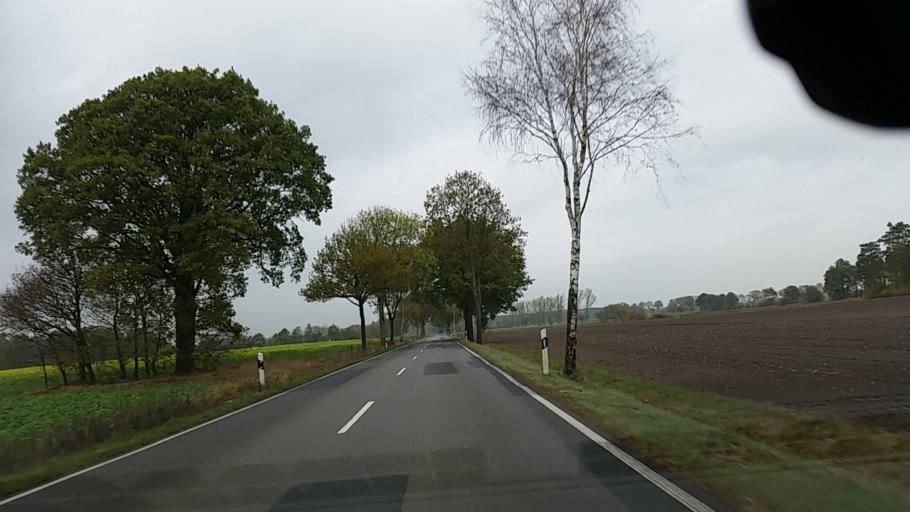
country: DE
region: Lower Saxony
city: Tulau
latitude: 52.6442
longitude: 10.8088
